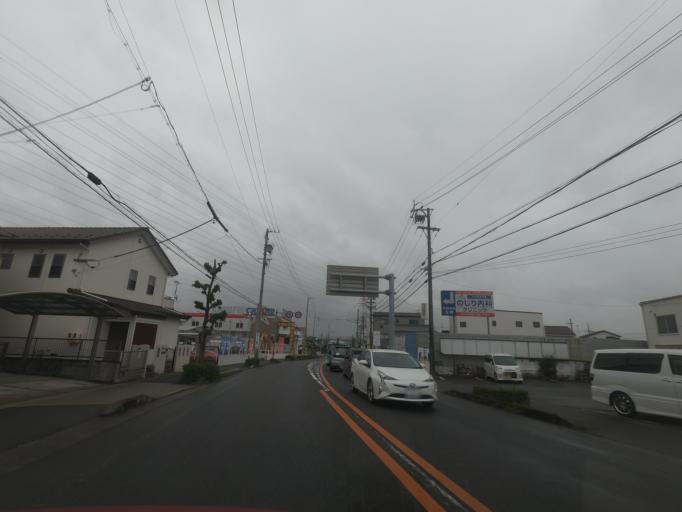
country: JP
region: Aichi
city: Kasugai
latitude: 35.2584
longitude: 136.9971
